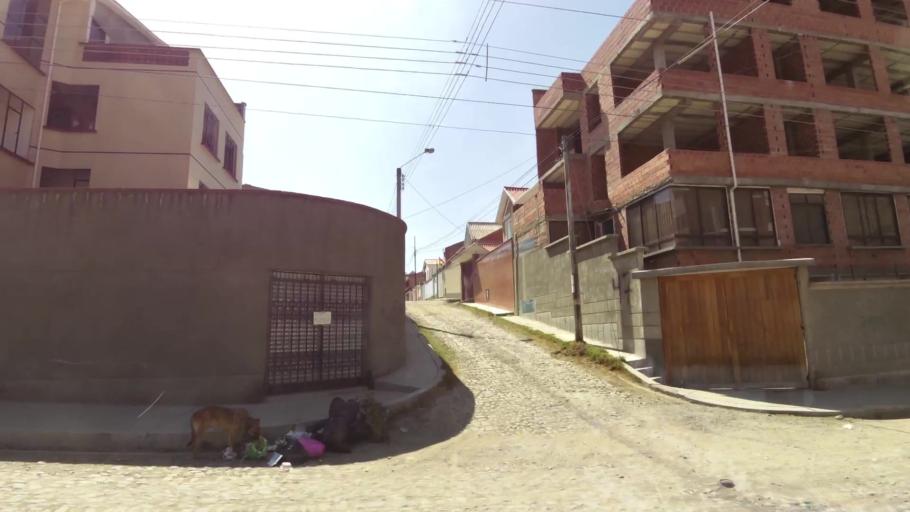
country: BO
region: La Paz
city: La Paz
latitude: -16.5402
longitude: -68.0515
